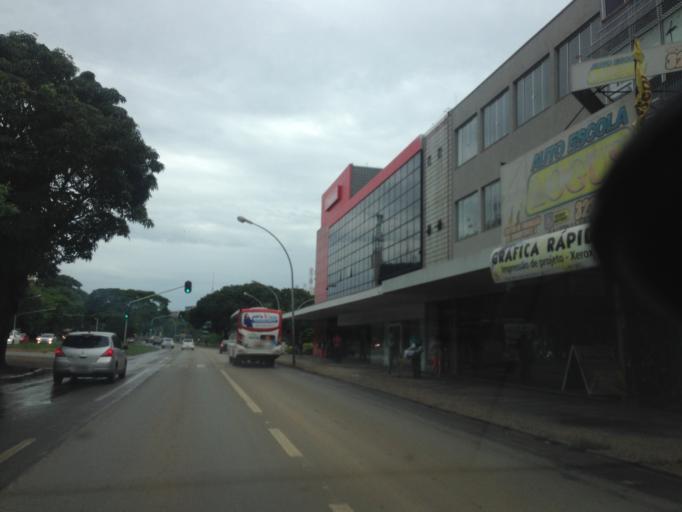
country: BR
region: Federal District
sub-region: Brasilia
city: Brasilia
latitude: -15.8004
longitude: -47.8935
